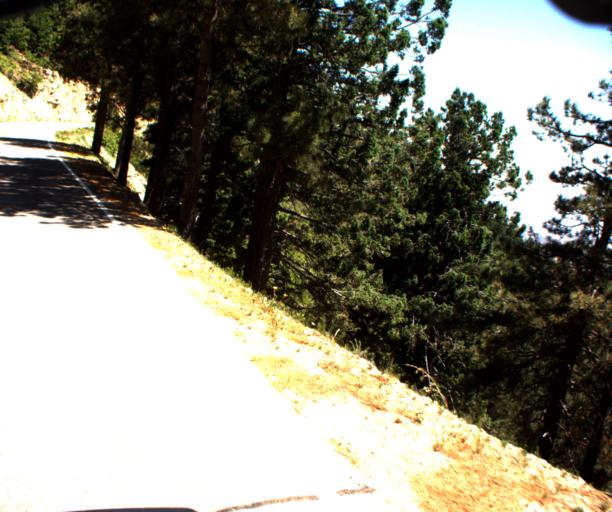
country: US
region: Arizona
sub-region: Graham County
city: Swift Trail Junction
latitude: 32.6386
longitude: -109.8491
